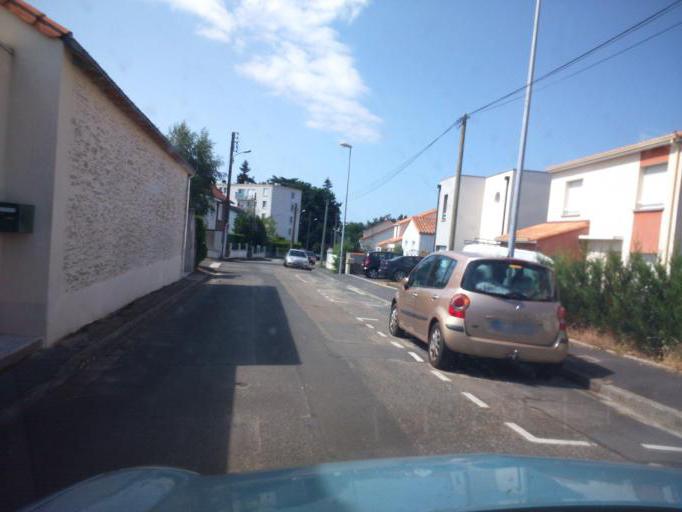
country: FR
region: Pays de la Loire
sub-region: Departement de la Loire-Atlantique
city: Saint-Sebastien-sur-Loire
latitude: 47.1942
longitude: -1.5217
